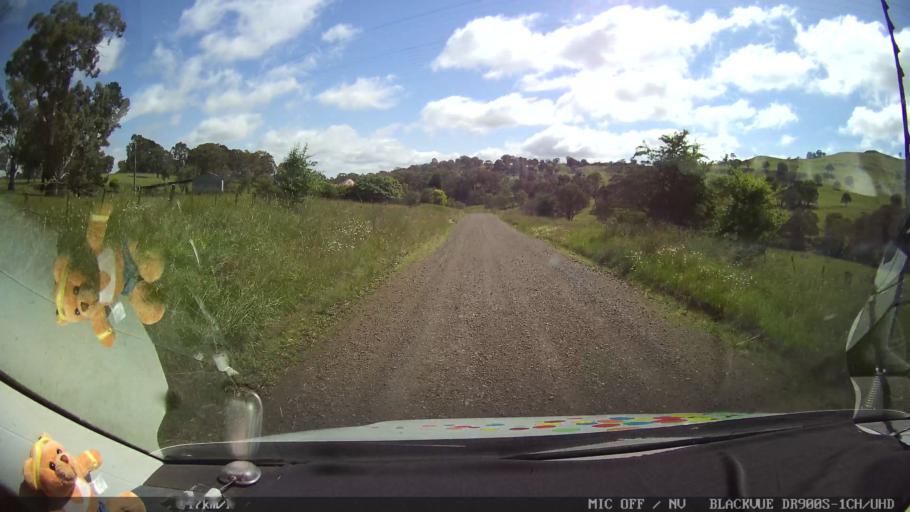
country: AU
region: New South Wales
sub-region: Guyra
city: Guyra
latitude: -29.9794
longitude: 151.6979
